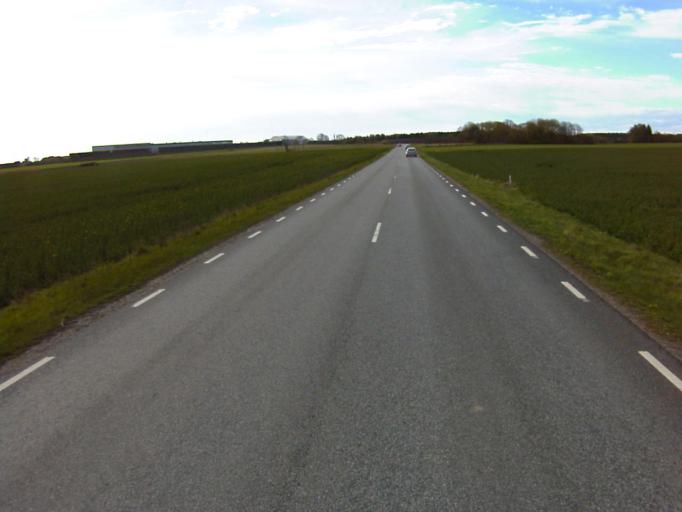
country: SE
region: Skane
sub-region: Kristianstads Kommun
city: Norra Asum
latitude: 55.9976
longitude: 14.1100
